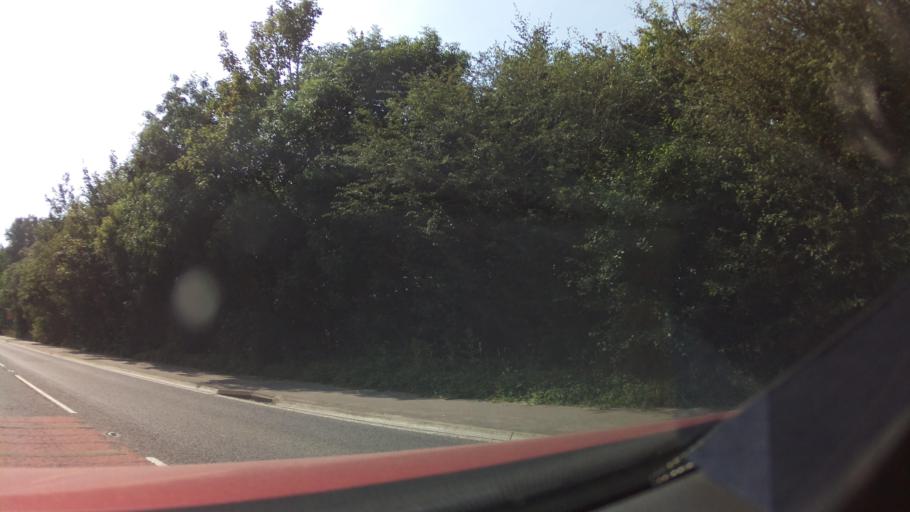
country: GB
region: England
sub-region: Wiltshire
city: Minety
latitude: 51.6552
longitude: -1.9341
